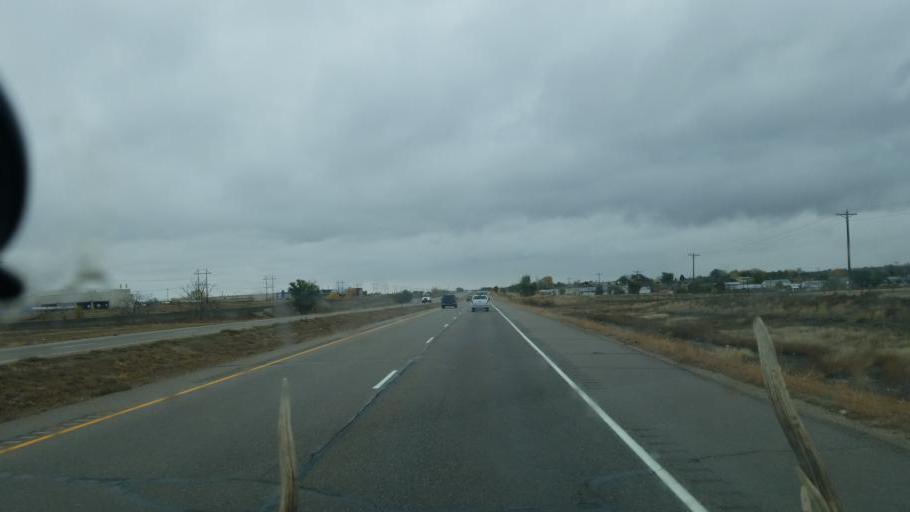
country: US
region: Colorado
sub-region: Pueblo County
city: Pueblo
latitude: 38.2743
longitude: -104.5289
